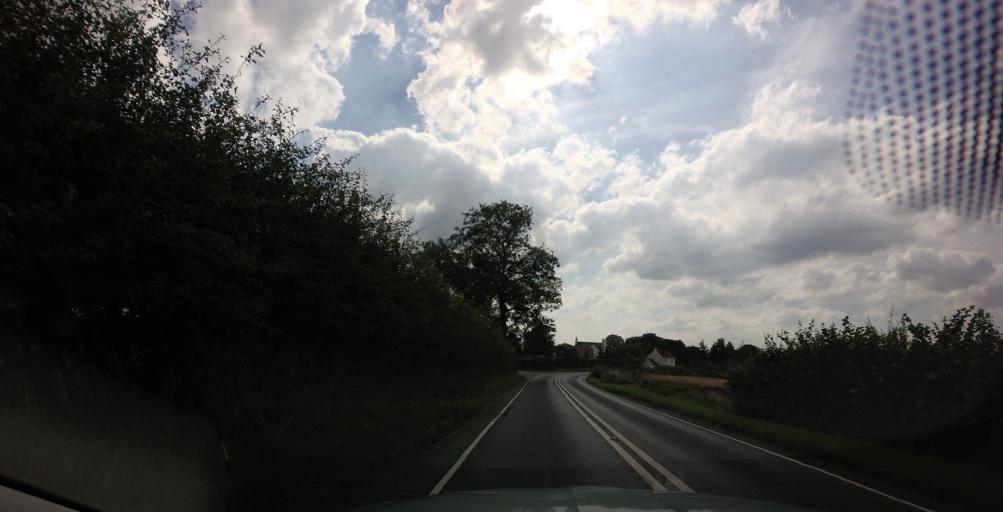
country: GB
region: England
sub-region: North Yorkshire
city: Ripon
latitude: 54.1273
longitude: -1.4874
